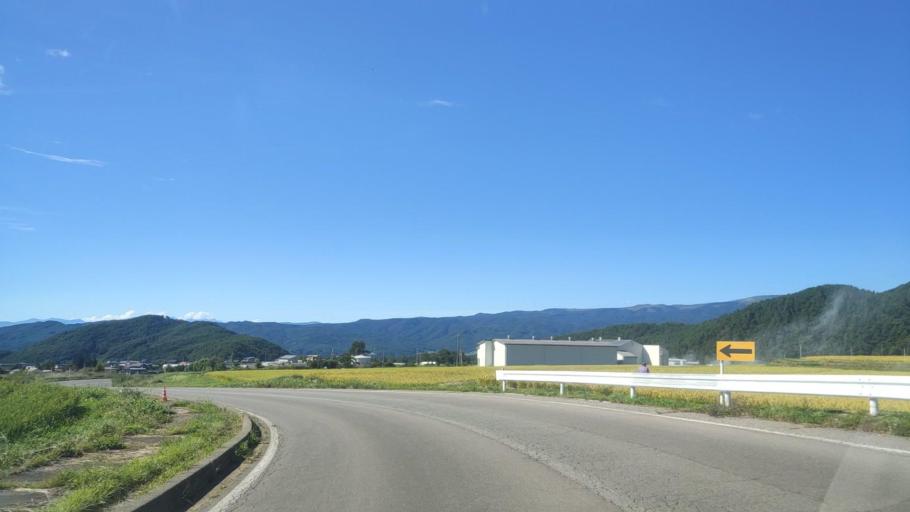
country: JP
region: Nagano
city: Chino
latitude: 35.9883
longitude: 138.2174
